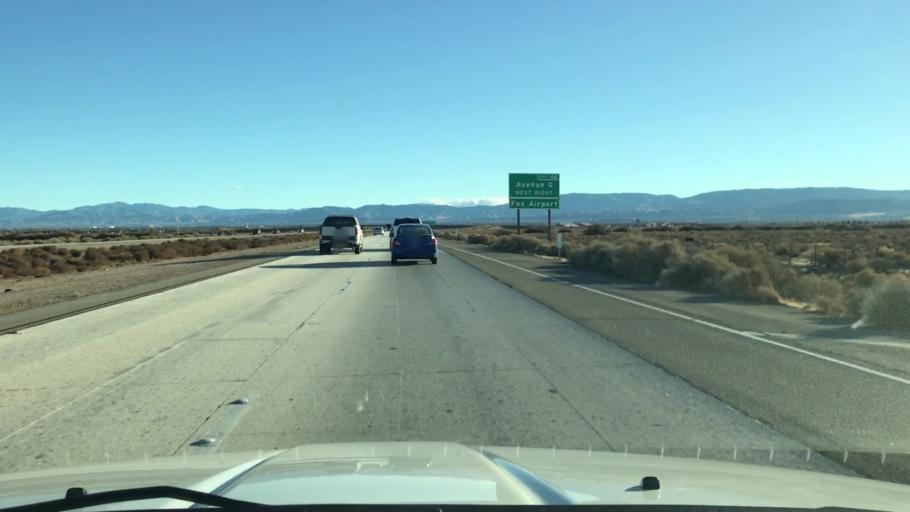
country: US
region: California
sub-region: Los Angeles County
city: Lancaster
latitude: 34.7436
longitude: -118.1706
